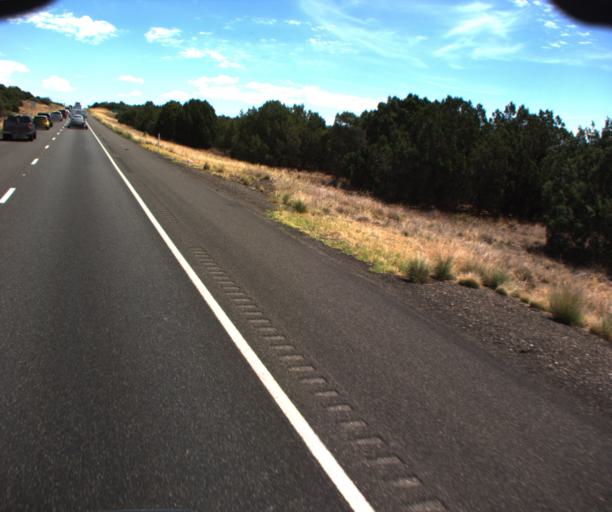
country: US
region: Arizona
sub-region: Yavapai County
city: Village of Oak Creek (Big Park)
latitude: 34.7398
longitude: -111.6913
